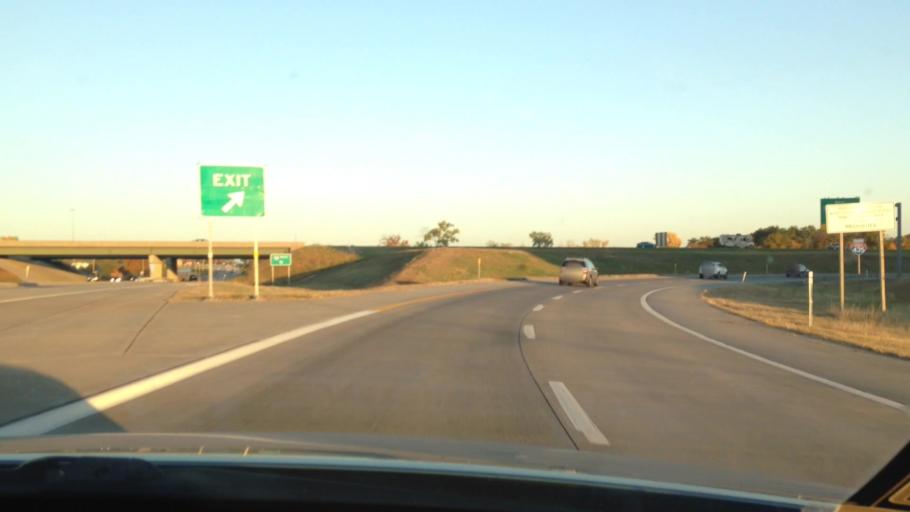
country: US
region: Kansas
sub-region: Wyandotte County
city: Edwardsville
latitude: 39.1161
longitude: -94.8143
